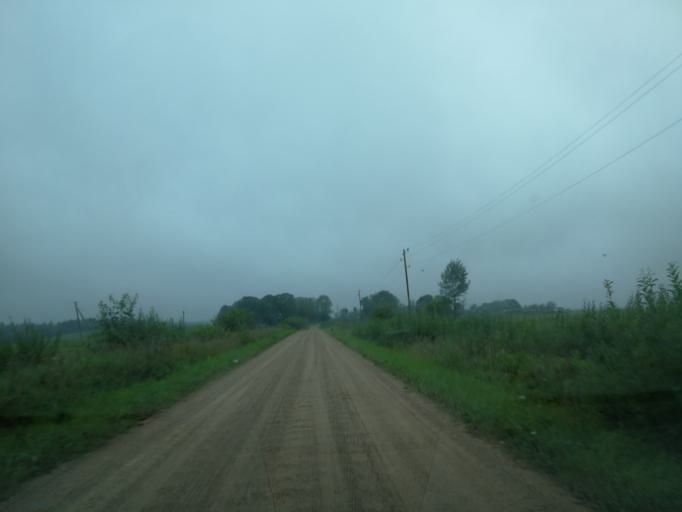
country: LV
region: Preilu Rajons
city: Jaunaglona
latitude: 56.3222
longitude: 27.0318
